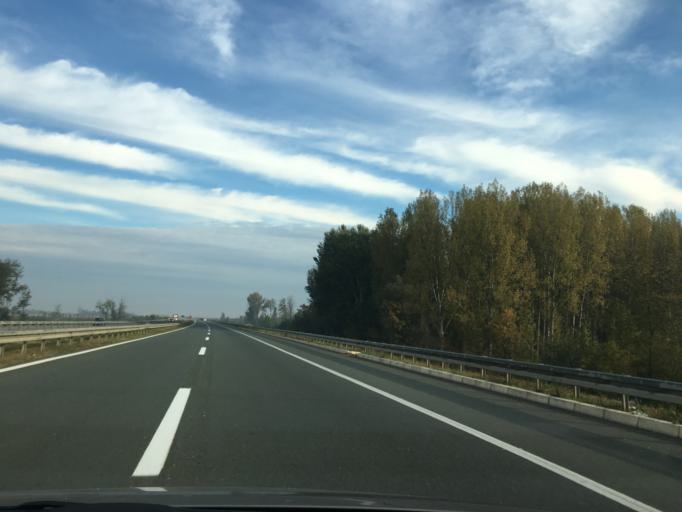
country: RS
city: Beska
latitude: 45.1882
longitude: 20.0768
